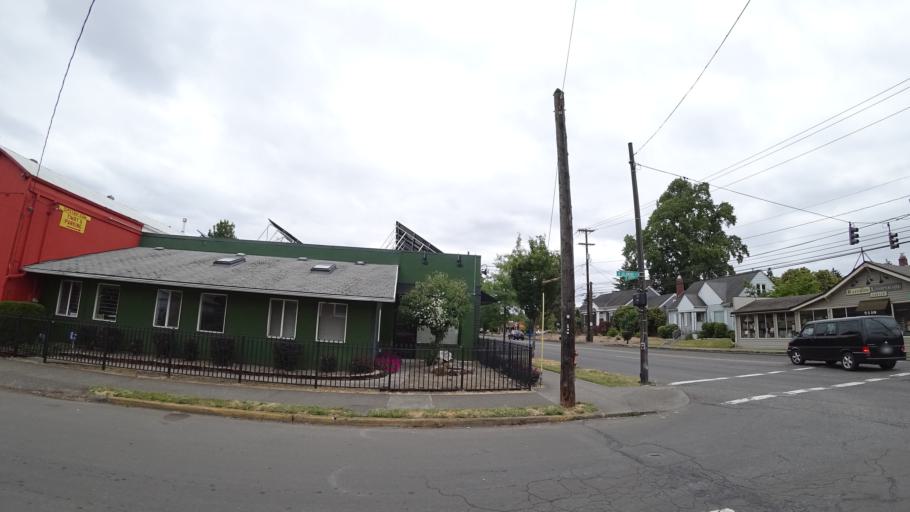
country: US
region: Oregon
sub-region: Multnomah County
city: Portland
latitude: 45.5773
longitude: -122.6925
